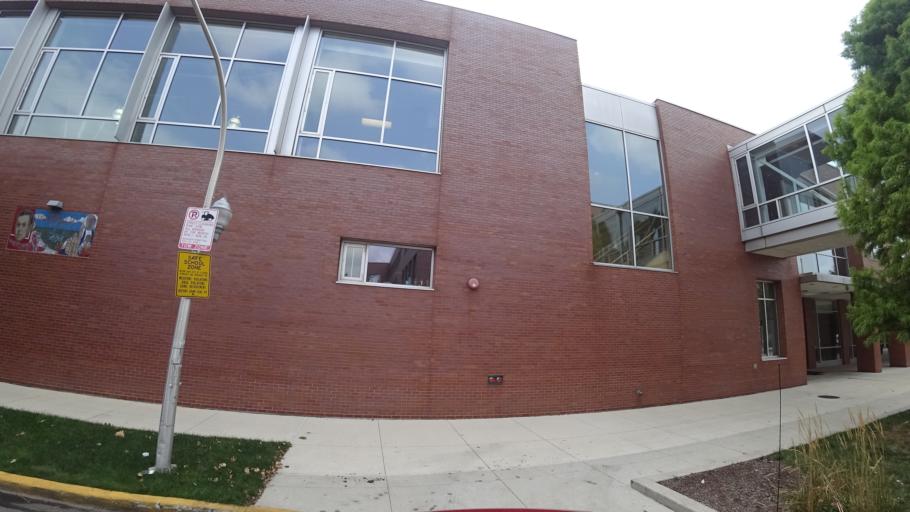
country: US
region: Illinois
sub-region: Cook County
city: Chicago
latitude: 41.8514
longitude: -87.6727
